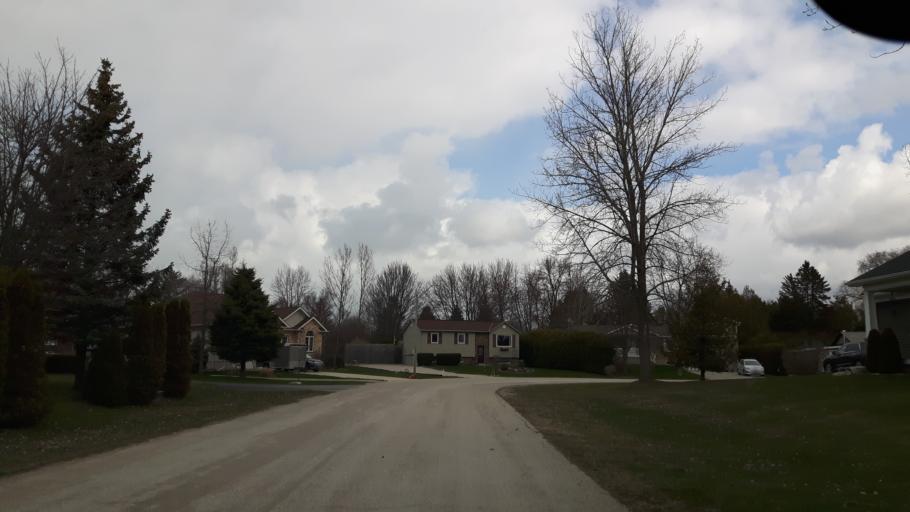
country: CA
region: Ontario
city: Bluewater
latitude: 43.5554
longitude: -81.7032
